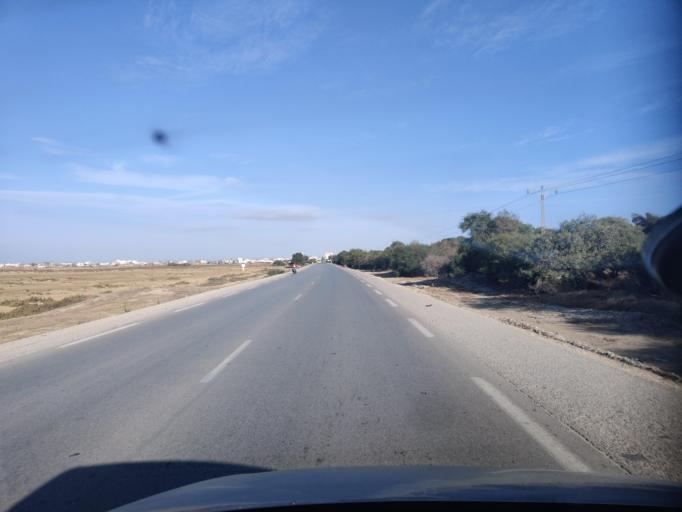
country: TN
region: Ariana
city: Ariana
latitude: 36.9491
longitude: 10.2391
